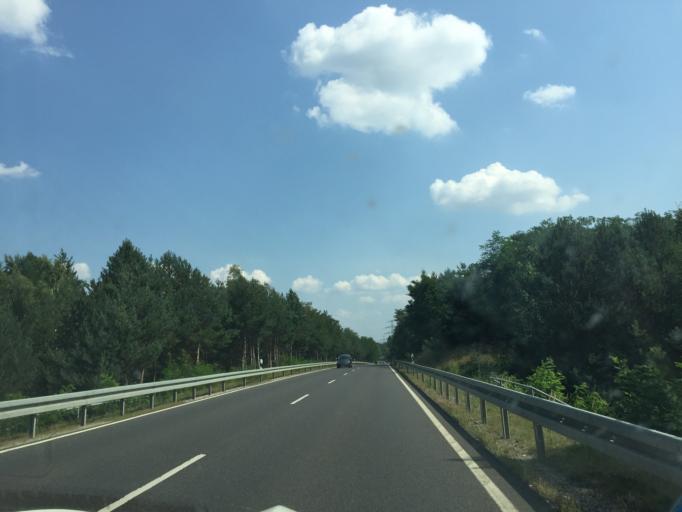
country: DE
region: Saxony
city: Boxberg
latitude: 51.4062
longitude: 14.5433
